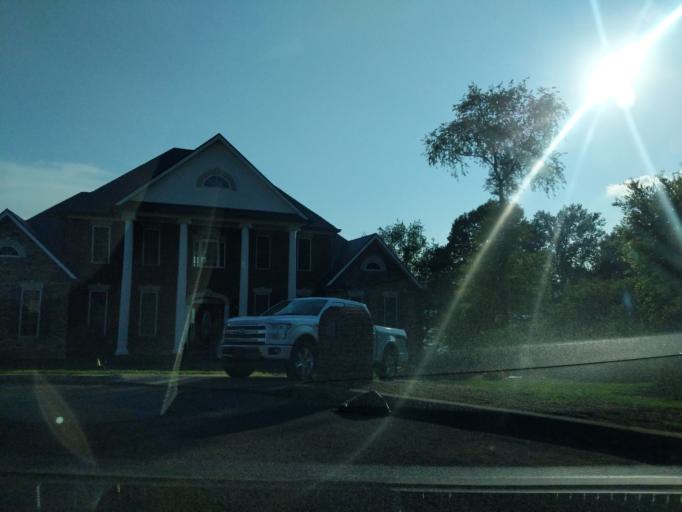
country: US
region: Tennessee
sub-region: Davidson County
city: Lakewood
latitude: 36.2601
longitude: -86.6322
